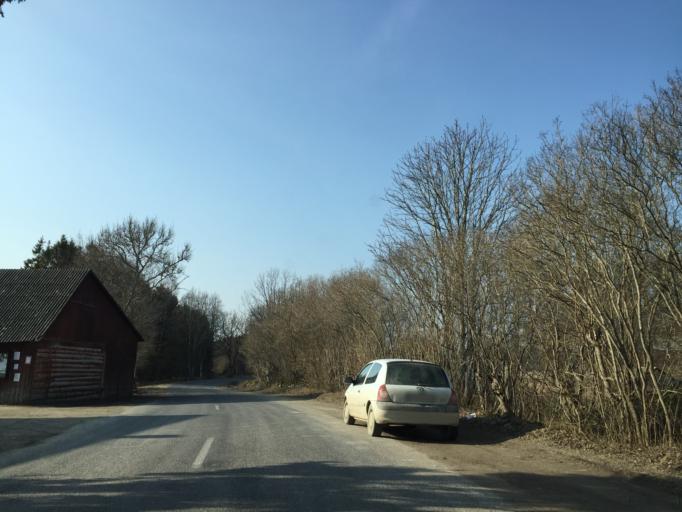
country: EE
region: Saare
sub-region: Orissaare vald
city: Orissaare
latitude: 58.6070
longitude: 23.3111
